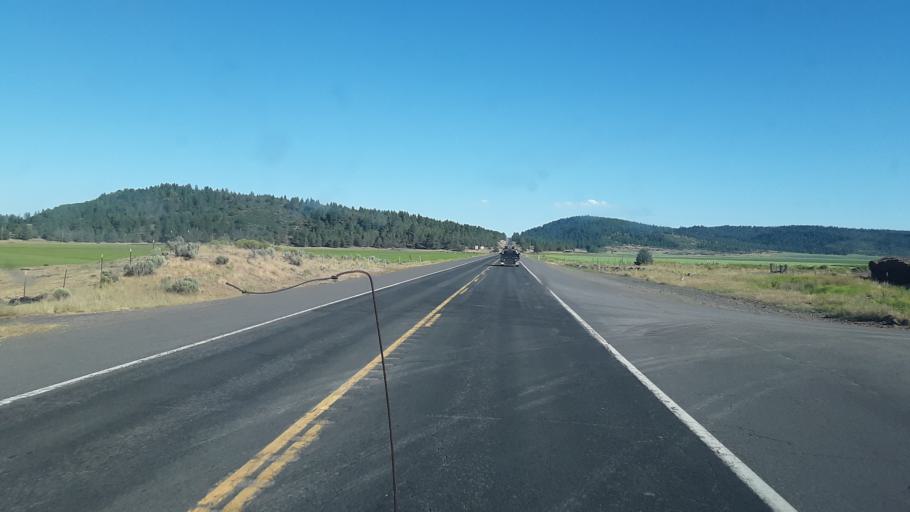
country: US
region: Oregon
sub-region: Klamath County
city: Klamath Falls
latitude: 42.2557
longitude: -121.8710
